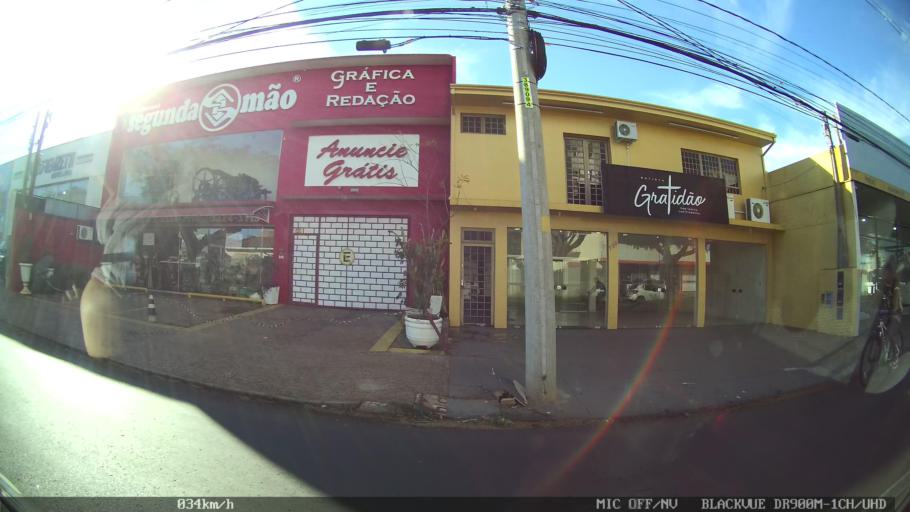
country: BR
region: Sao Paulo
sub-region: Araraquara
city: Araraquara
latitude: -21.7681
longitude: -48.1678
